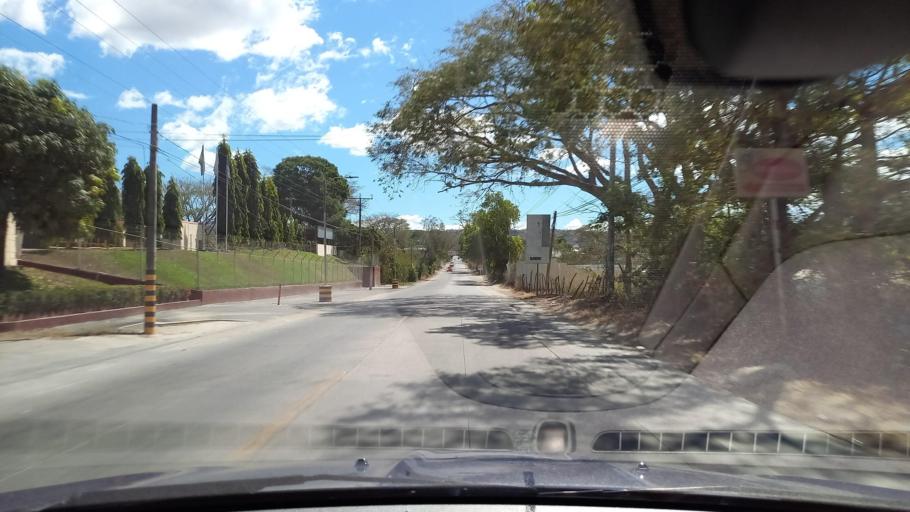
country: SV
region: Santa Ana
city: Metapan
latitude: 14.3409
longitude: -89.4515
